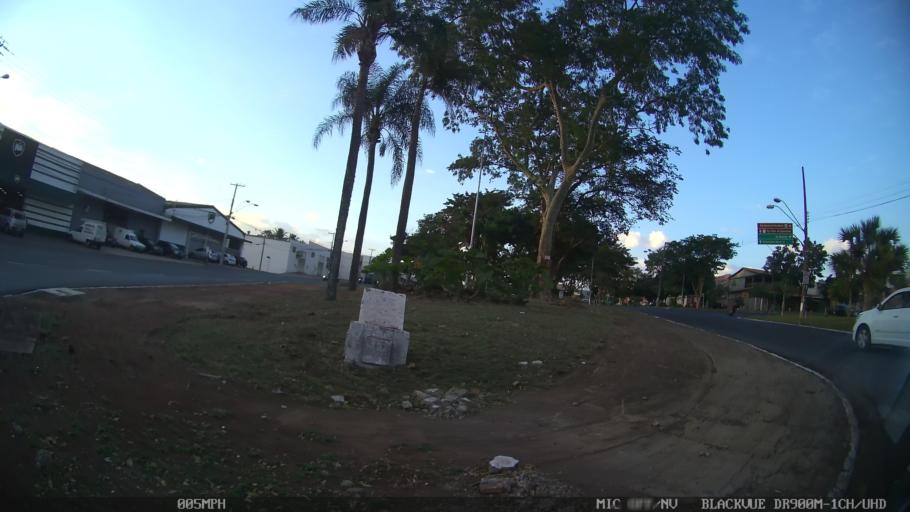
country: BR
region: Sao Paulo
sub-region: Ribeirao Preto
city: Ribeirao Preto
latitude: -21.1431
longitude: -47.7995
